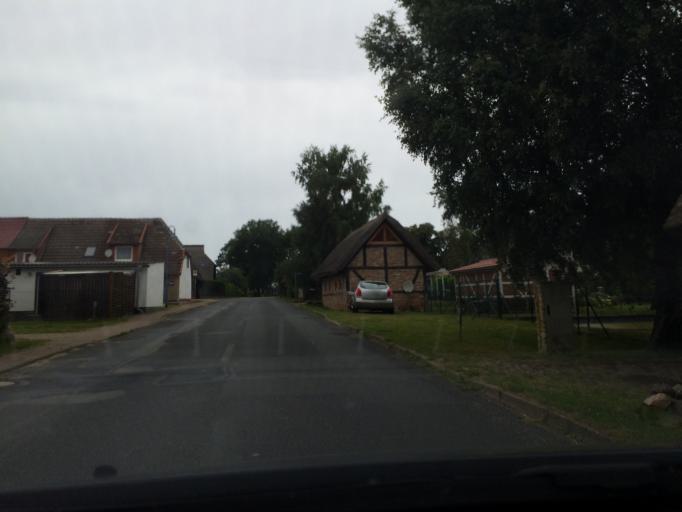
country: DE
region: Mecklenburg-Vorpommern
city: Prohn
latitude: 54.4124
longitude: 13.0159
